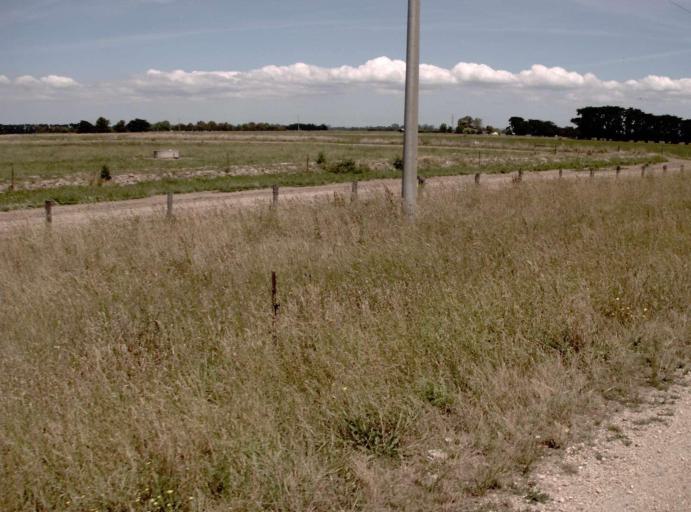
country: AU
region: Victoria
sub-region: Wellington
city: Heyfield
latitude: -37.9867
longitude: 146.8871
